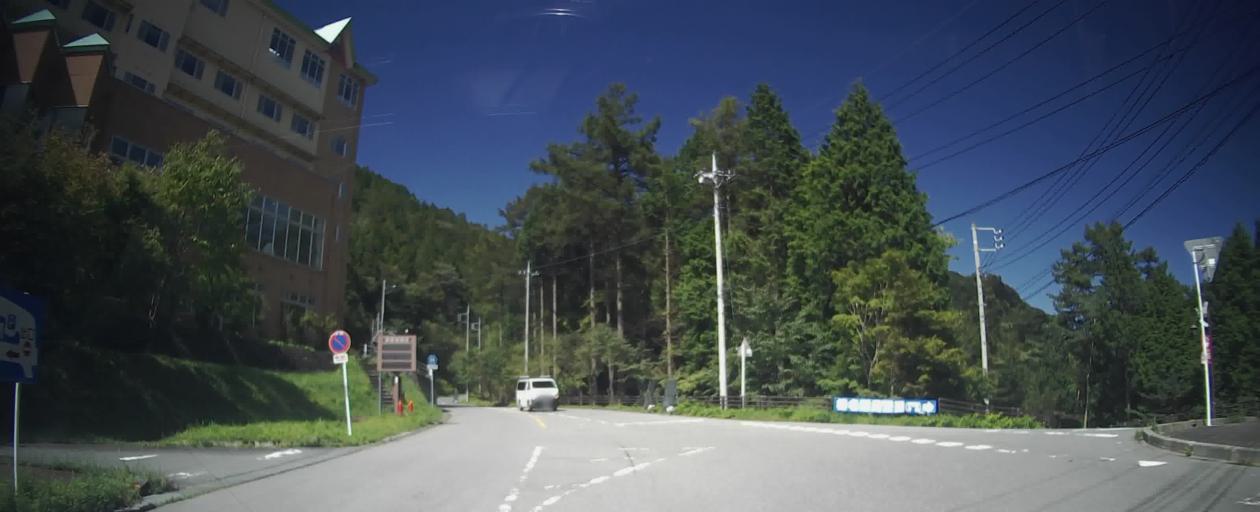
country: JP
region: Gunma
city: Nakanojomachi
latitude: 36.4772
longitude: 138.8608
